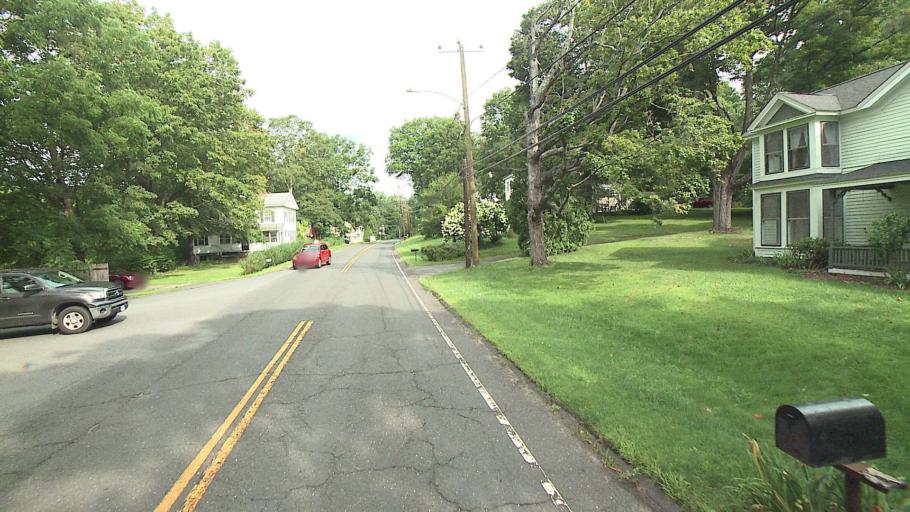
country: US
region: Connecticut
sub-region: Litchfield County
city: Woodbury
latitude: 41.5591
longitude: -73.2137
